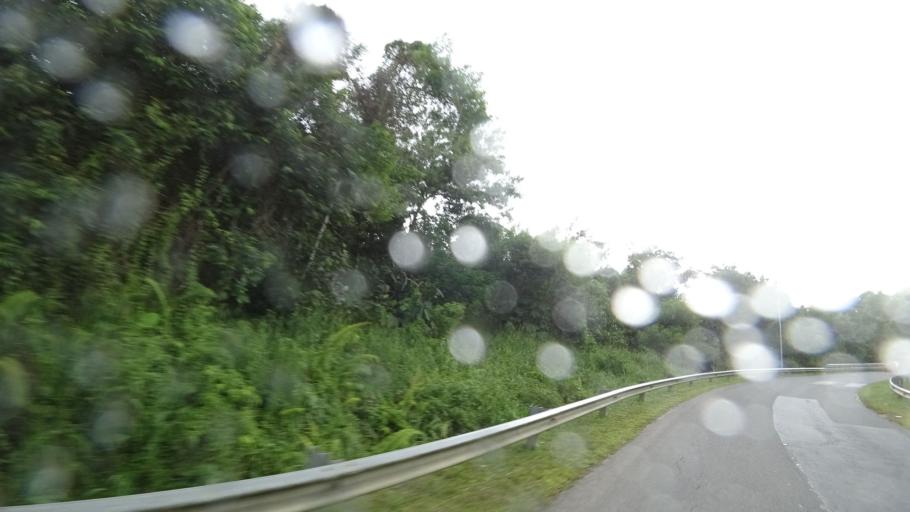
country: BN
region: Brunei and Muara
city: Bandar Seri Begawan
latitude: 4.8619
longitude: 114.9476
